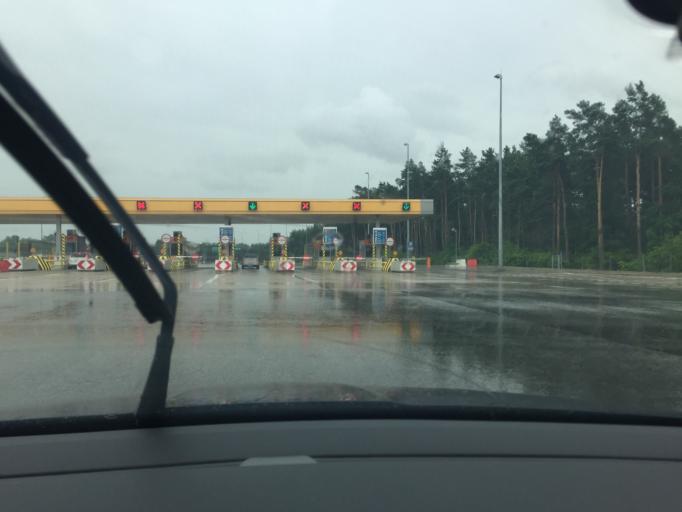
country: PL
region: Kujawsko-Pomorskie
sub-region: Powiat torunski
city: Lubicz Dolny
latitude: 53.0358
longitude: 18.7365
